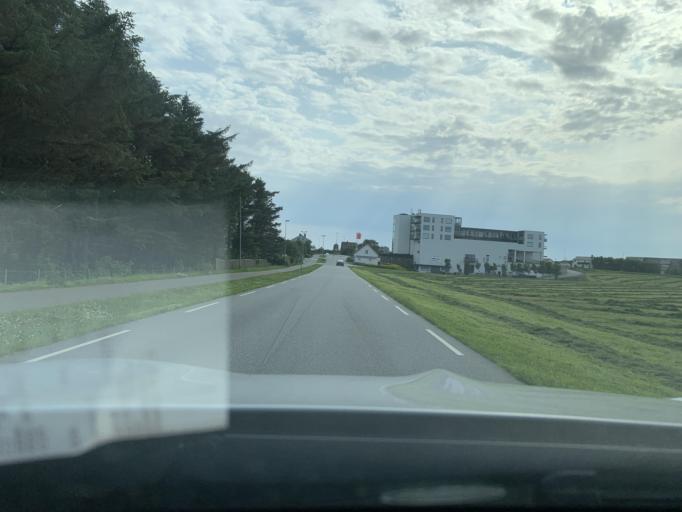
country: NO
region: Rogaland
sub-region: Time
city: Bryne
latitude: 58.7198
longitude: 5.5714
